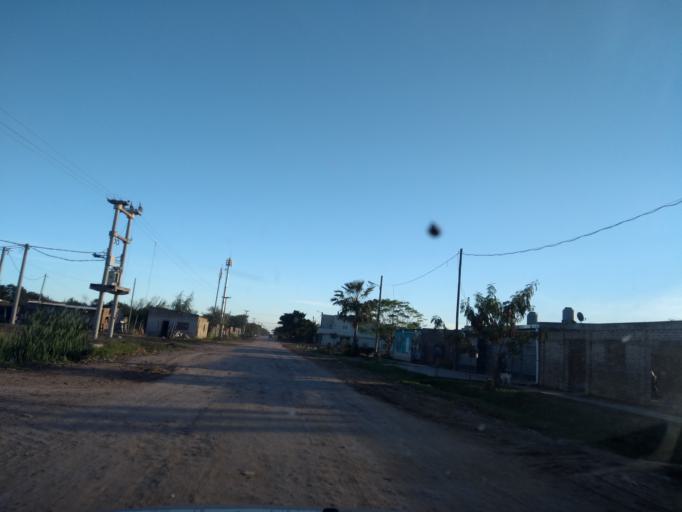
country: AR
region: Chaco
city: Puerto Vilelas
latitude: -27.4961
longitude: -58.9653
